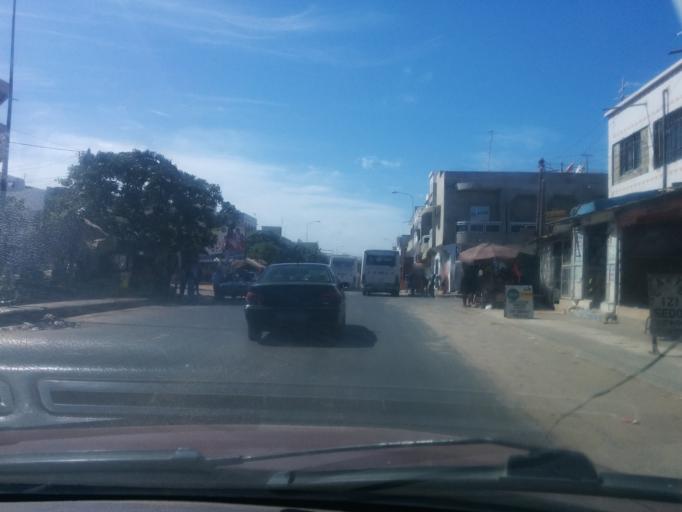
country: SN
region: Dakar
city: Pikine
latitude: 14.7804
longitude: -17.3893
